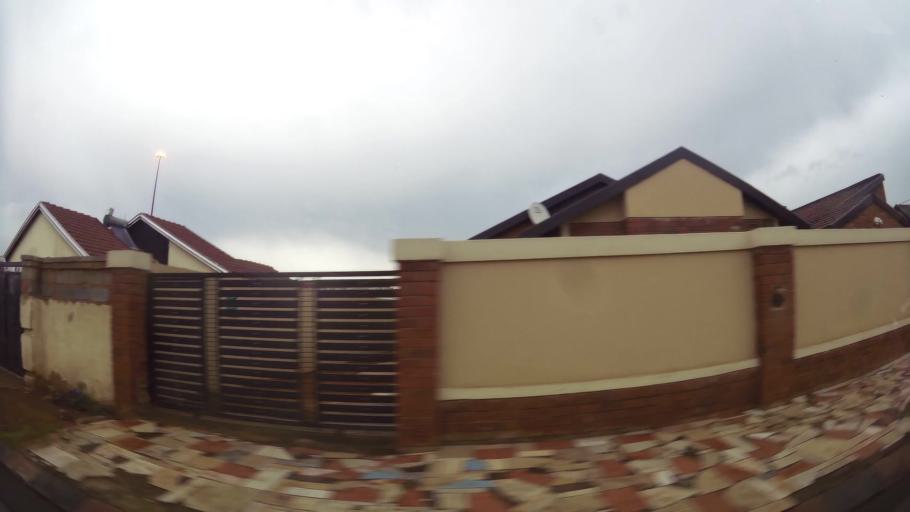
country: ZA
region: Gauteng
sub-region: Ekurhuleni Metropolitan Municipality
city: Germiston
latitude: -26.3355
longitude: 28.1979
